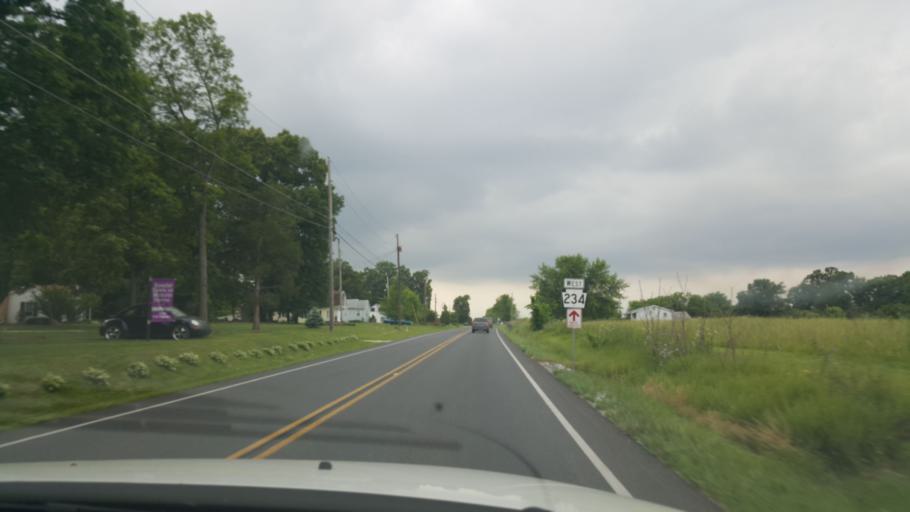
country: US
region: Pennsylvania
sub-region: Adams County
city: Lake Meade
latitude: 39.9487
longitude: -77.1032
